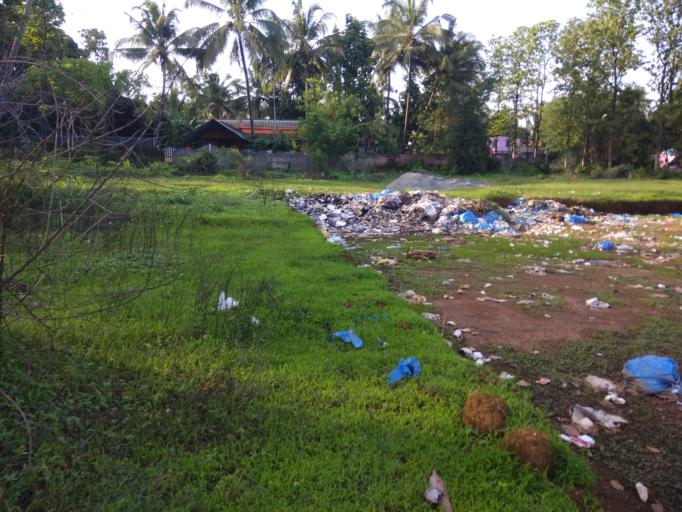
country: IN
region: Kerala
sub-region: Thrissur District
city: Avanoor
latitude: 10.5603
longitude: 76.1749
